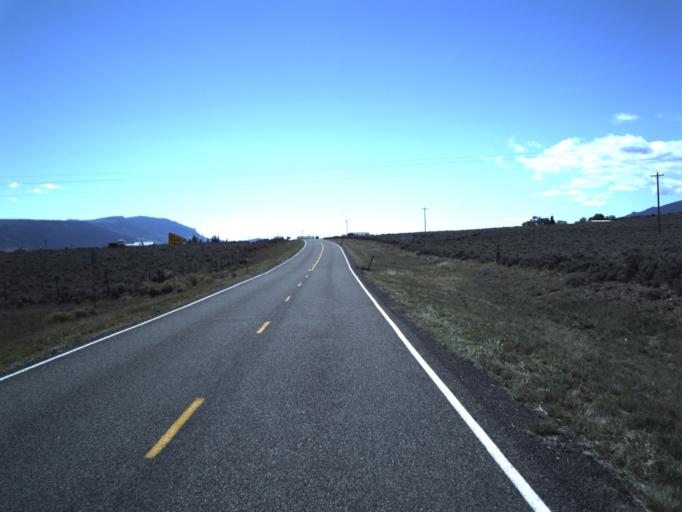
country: US
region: Utah
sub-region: Sevier County
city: Monroe
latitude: 38.5274
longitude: -111.8800
